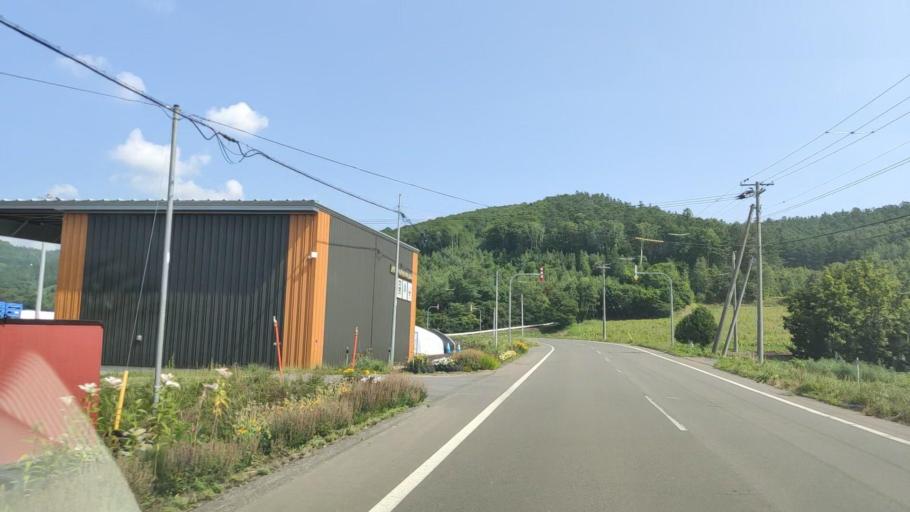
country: JP
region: Hokkaido
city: Shimo-furano
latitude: 43.4185
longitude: 142.4016
